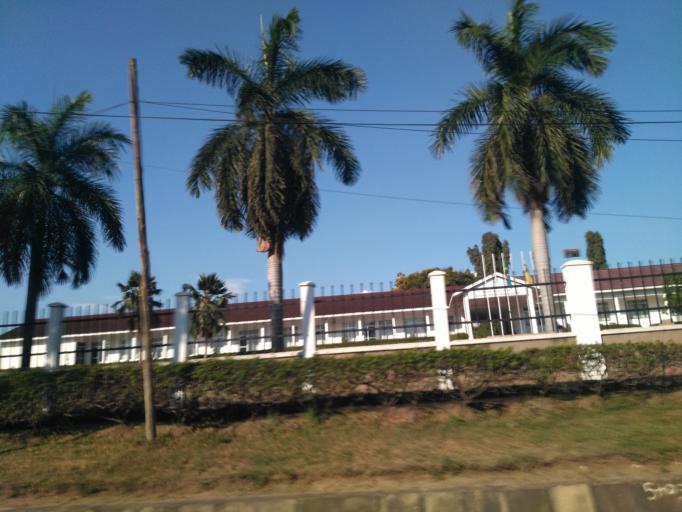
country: TZ
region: Dar es Salaam
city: Magomeni
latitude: -6.7465
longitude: 39.2398
